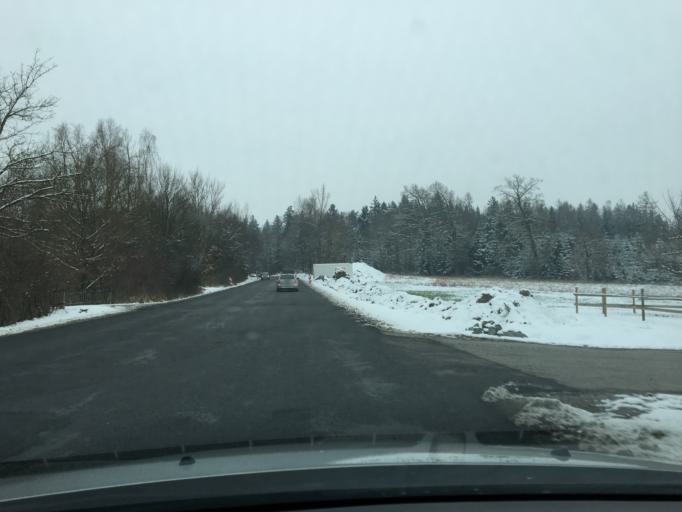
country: DE
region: Bavaria
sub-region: Upper Bavaria
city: Egglkofen
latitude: 48.4039
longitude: 12.4443
